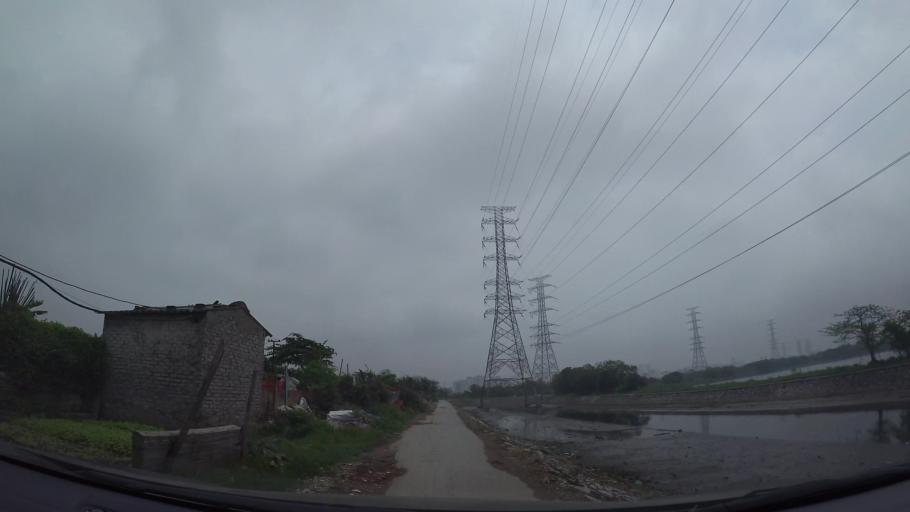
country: VN
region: Ha Noi
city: Van Dien
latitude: 20.9724
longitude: 105.8541
